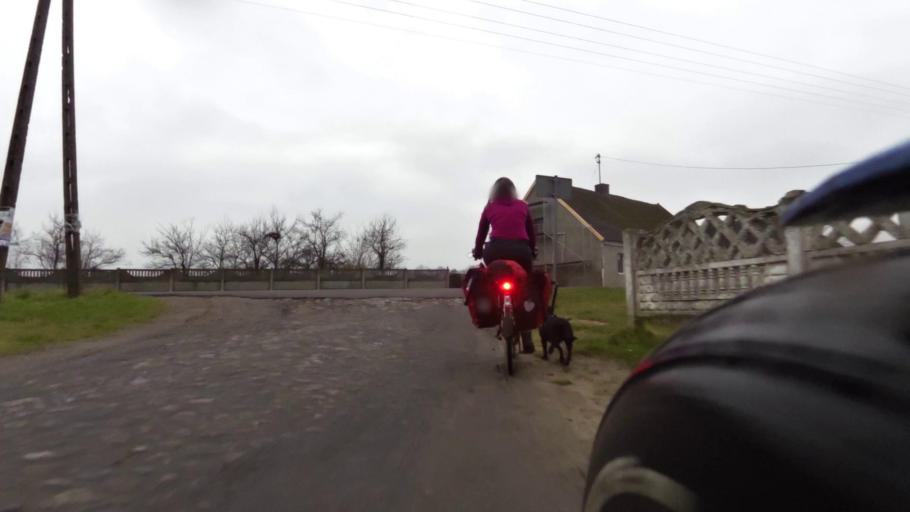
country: PL
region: West Pomeranian Voivodeship
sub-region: Powiat szczecinecki
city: Szczecinek
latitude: 53.6604
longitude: 16.6688
